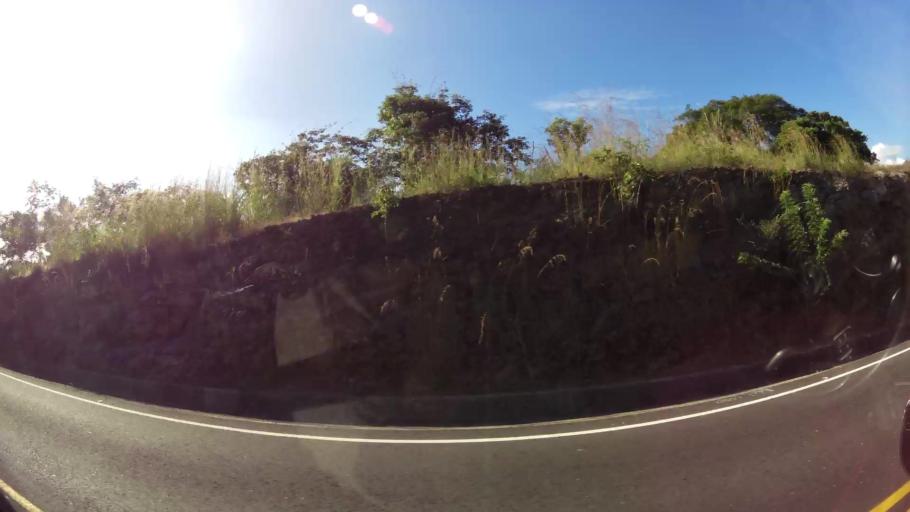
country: CR
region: Guanacaste
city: Sardinal
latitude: 10.5854
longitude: -85.6374
